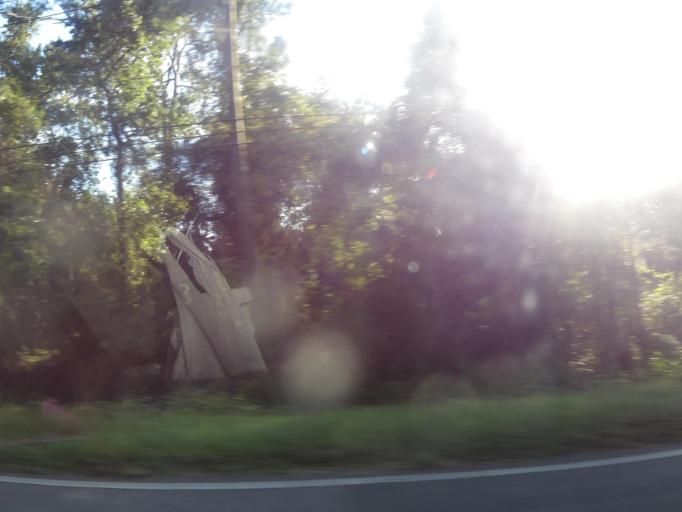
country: US
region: Florida
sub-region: Clay County
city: Green Cove Springs
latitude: 29.9081
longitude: -81.5126
